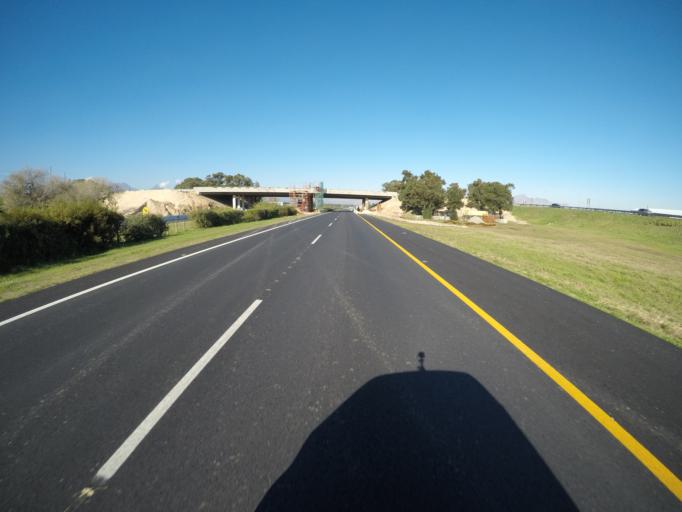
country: ZA
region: Western Cape
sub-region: Cape Winelands District Municipality
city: Stellenbosch
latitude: -34.0764
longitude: 18.8200
